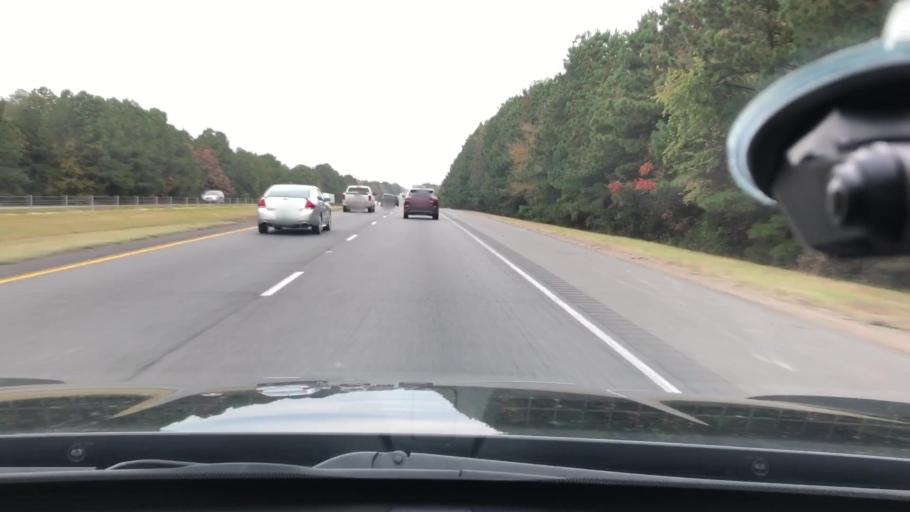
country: US
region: Arkansas
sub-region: Clark County
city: Arkadelphia
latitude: 34.0453
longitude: -93.1374
